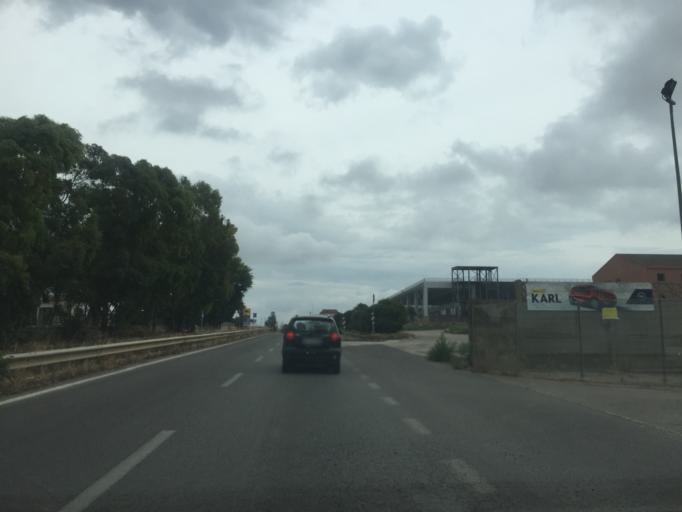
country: IT
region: Sicily
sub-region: Ragusa
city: Ragusa
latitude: 36.8847
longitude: 14.6841
